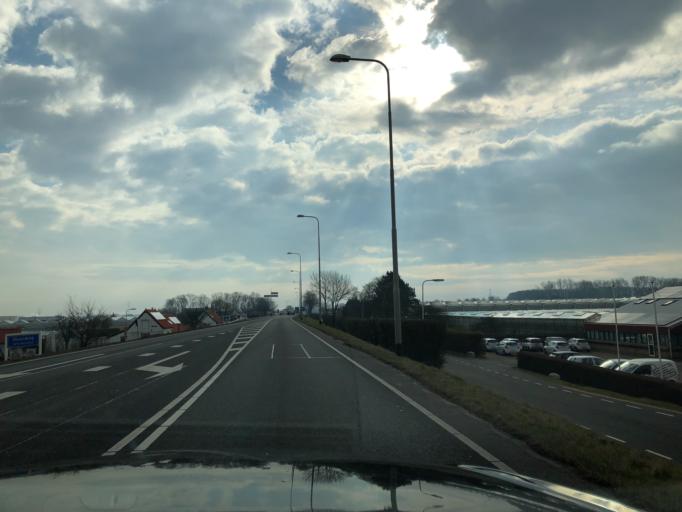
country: NL
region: South Holland
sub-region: Gemeente Westland
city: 's-Gravenzande
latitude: 51.9804
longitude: 4.1804
